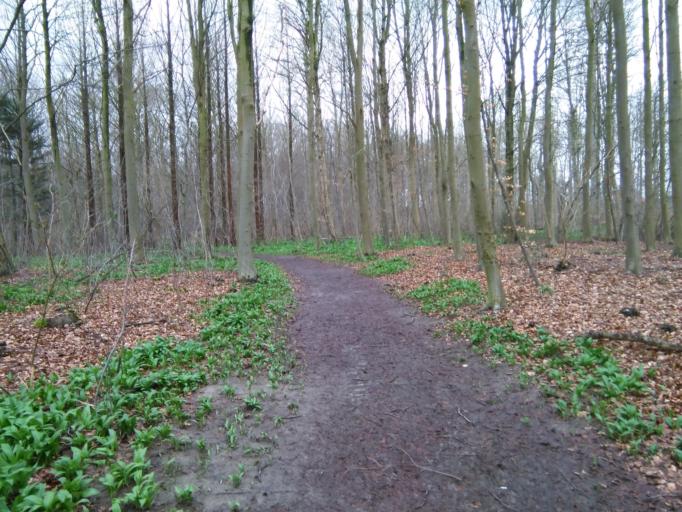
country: DK
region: Central Jutland
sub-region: Arhus Kommune
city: Arhus
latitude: 56.1814
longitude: 10.2224
